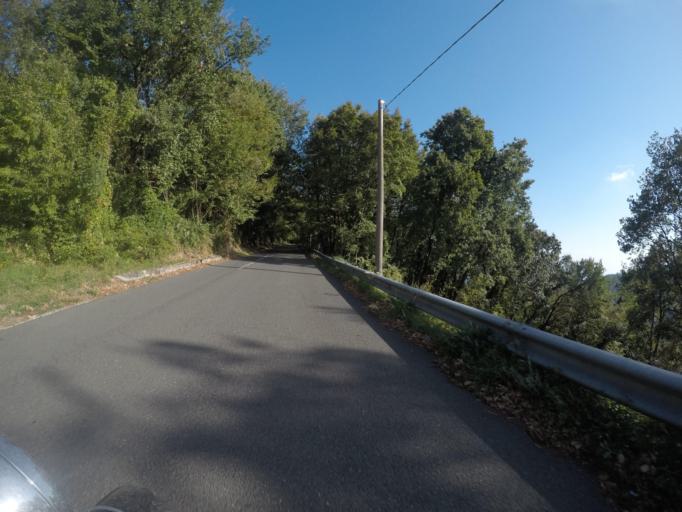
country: IT
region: Tuscany
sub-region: Provincia di Massa-Carrara
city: Massa
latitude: 44.0696
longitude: 10.1168
